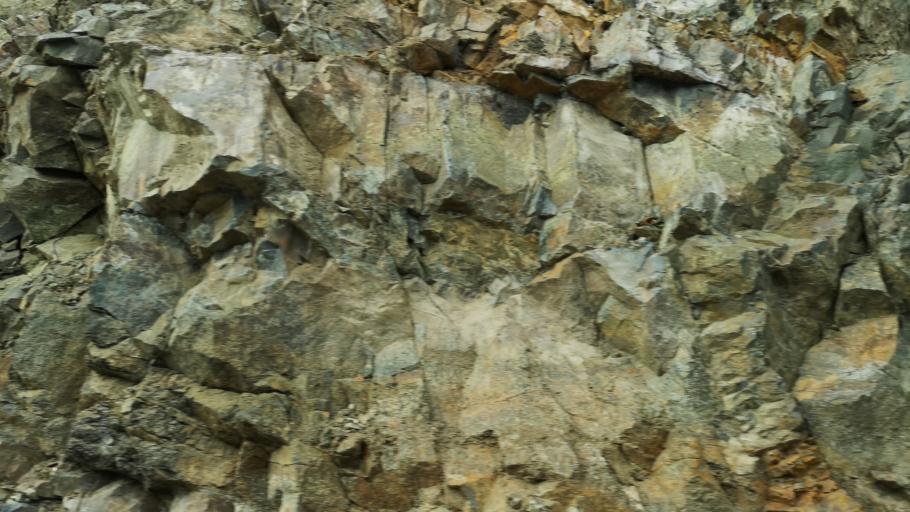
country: ES
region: Canary Islands
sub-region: Provincia de Santa Cruz de Tenerife
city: Vallehermosa
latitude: 28.2010
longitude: -17.2557
